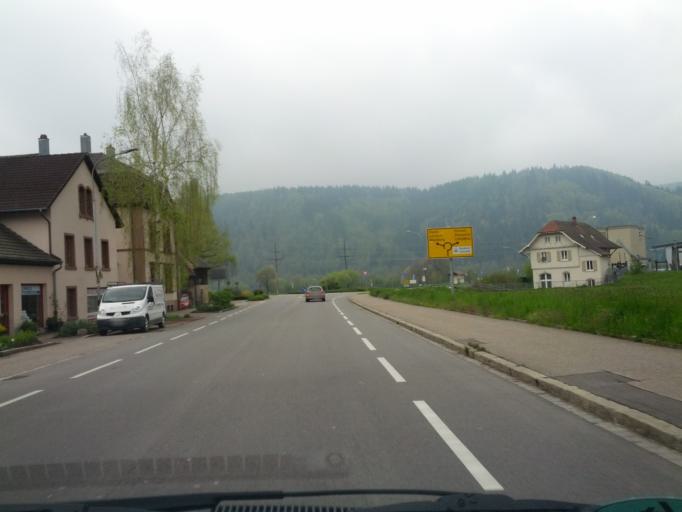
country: DE
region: Baden-Wuerttemberg
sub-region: Freiburg Region
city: Schopfheim
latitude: 47.6482
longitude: 7.8018
